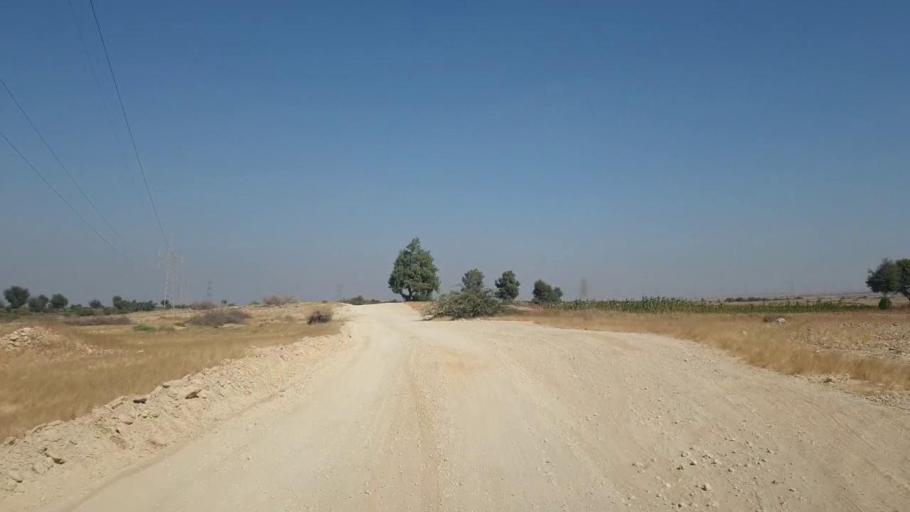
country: PK
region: Sindh
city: Thatta
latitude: 25.2484
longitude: 67.8048
